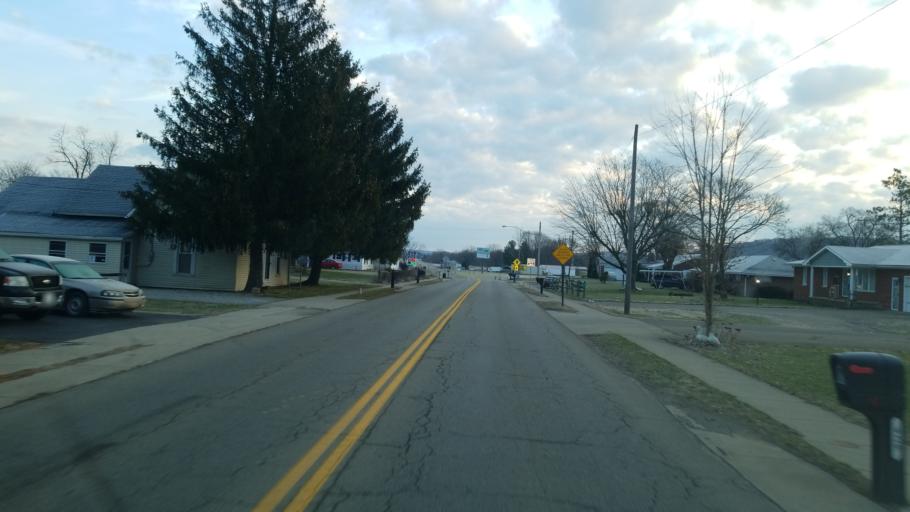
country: US
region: Ohio
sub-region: Highland County
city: Greenfield
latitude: 39.2294
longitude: -83.2617
